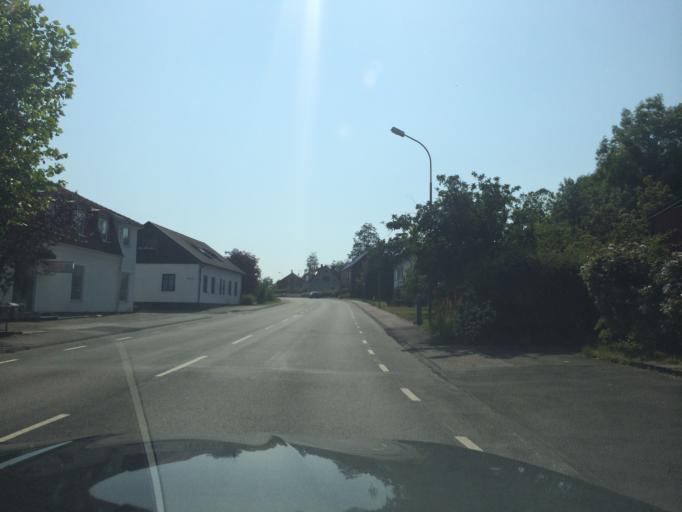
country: SE
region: Skane
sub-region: Simrishamns Kommun
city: Kivik
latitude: 55.6368
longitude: 14.1311
